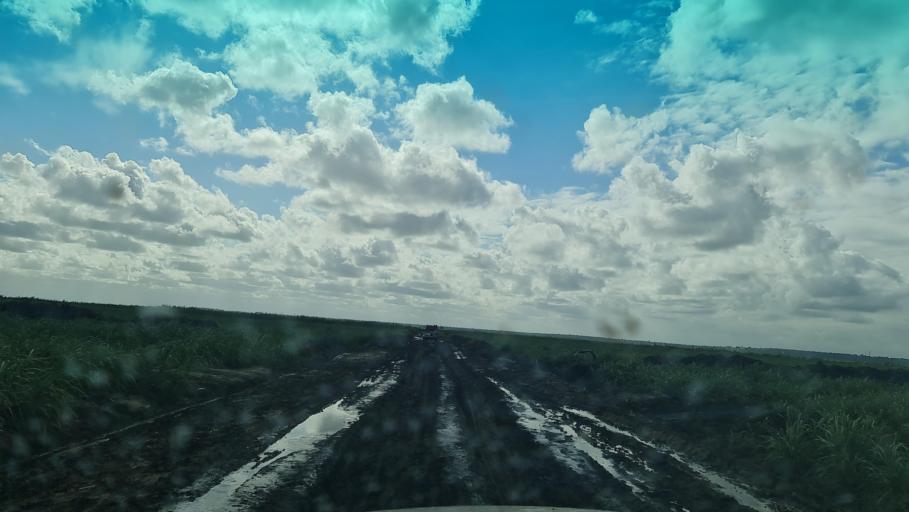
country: MZ
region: Maputo
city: Manhica
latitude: -25.4389
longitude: 32.8549
